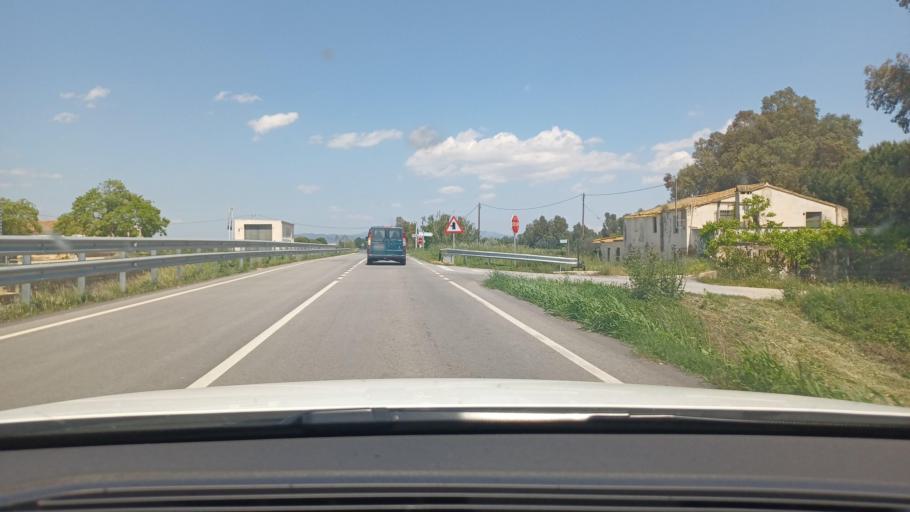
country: ES
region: Catalonia
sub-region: Provincia de Tarragona
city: Amposta
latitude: 40.6702
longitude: 0.5907
